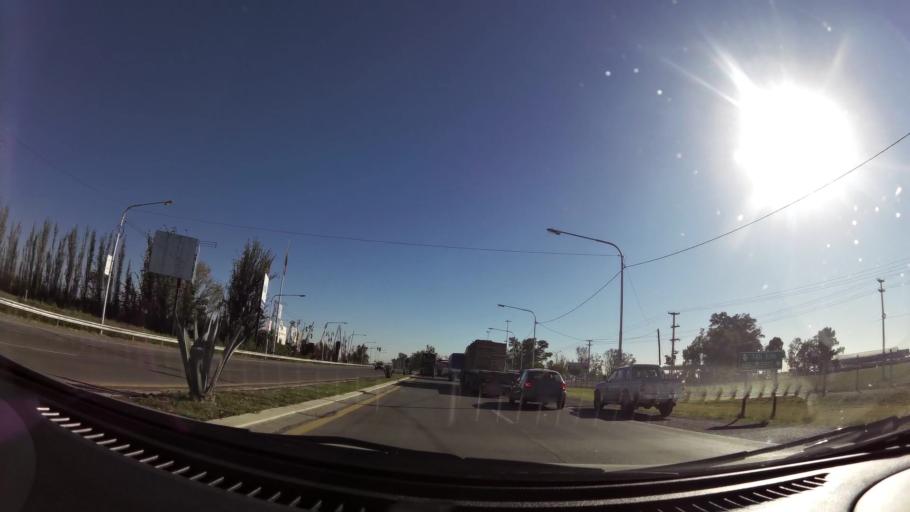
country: AR
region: Mendoza
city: Las Heras
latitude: -32.8287
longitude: -68.8051
